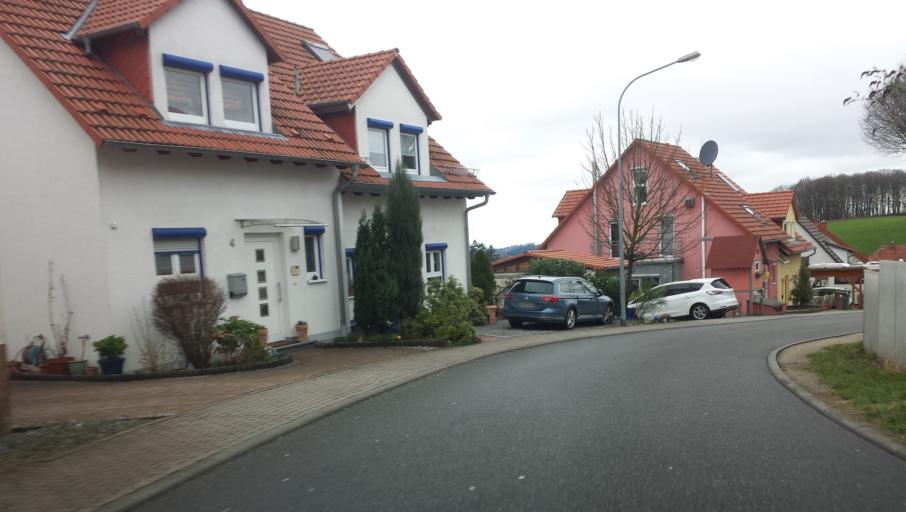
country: DE
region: Hesse
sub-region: Regierungsbezirk Darmstadt
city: Birkenau
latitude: 49.5450
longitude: 8.7323
